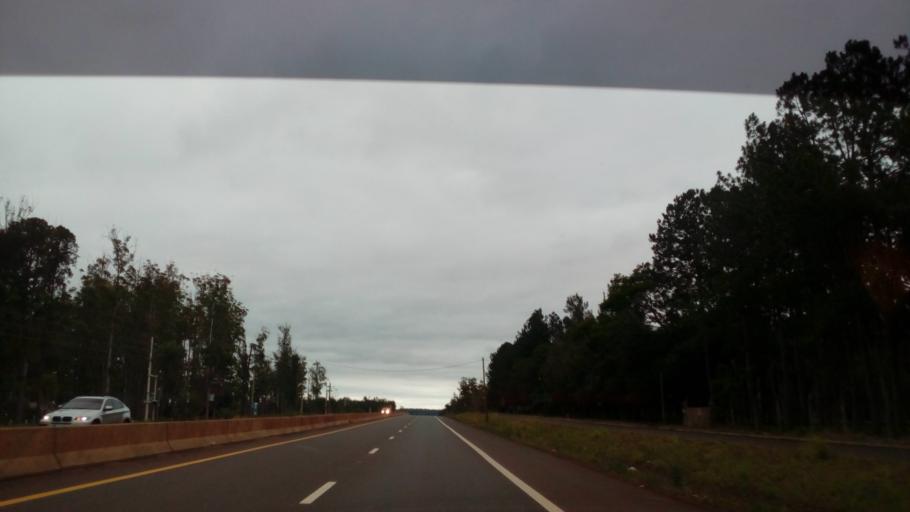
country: AR
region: Misiones
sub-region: Departamento de Candelaria
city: Candelaria
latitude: -27.4680
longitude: -55.7826
